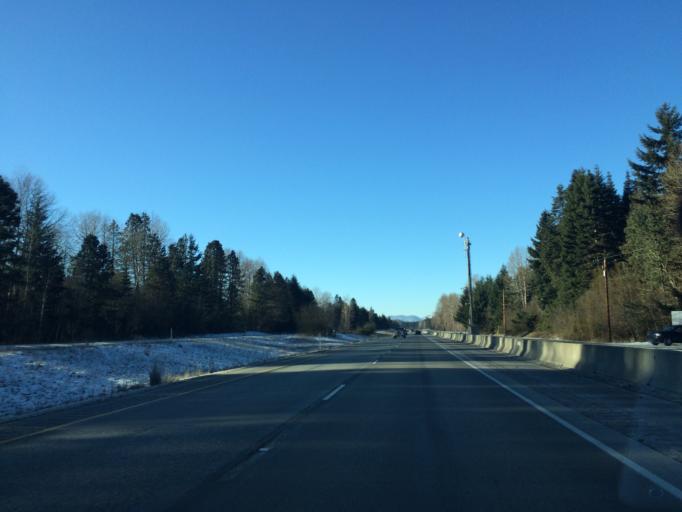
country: US
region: Washington
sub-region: Kittitas County
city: Cle Elum
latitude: 47.2047
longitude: -121.0818
